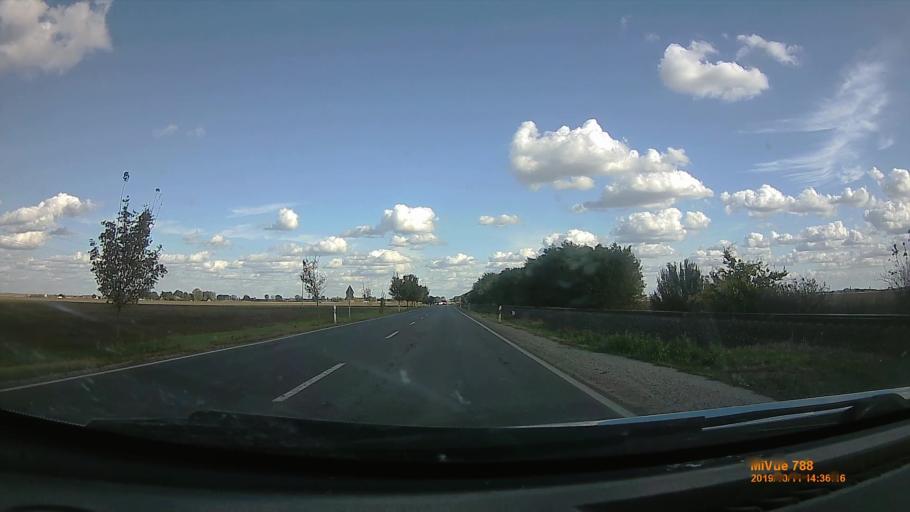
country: HU
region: Hajdu-Bihar
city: Ebes
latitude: 47.5572
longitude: 21.5058
